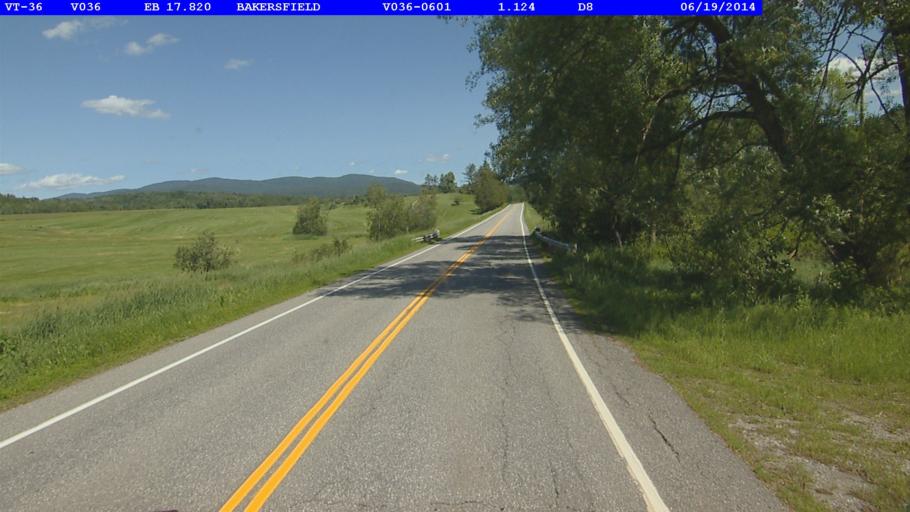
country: US
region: Vermont
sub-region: Franklin County
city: Enosburg Falls
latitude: 44.7832
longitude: -72.8280
